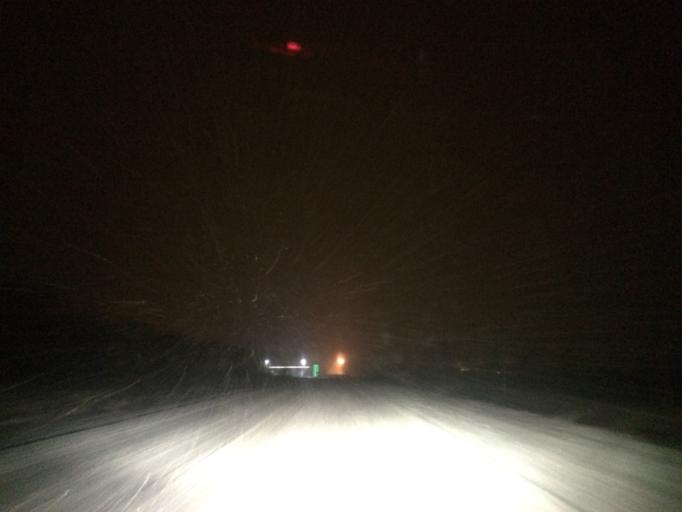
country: RU
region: Tula
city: Dubna
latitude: 54.0972
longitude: 37.1006
